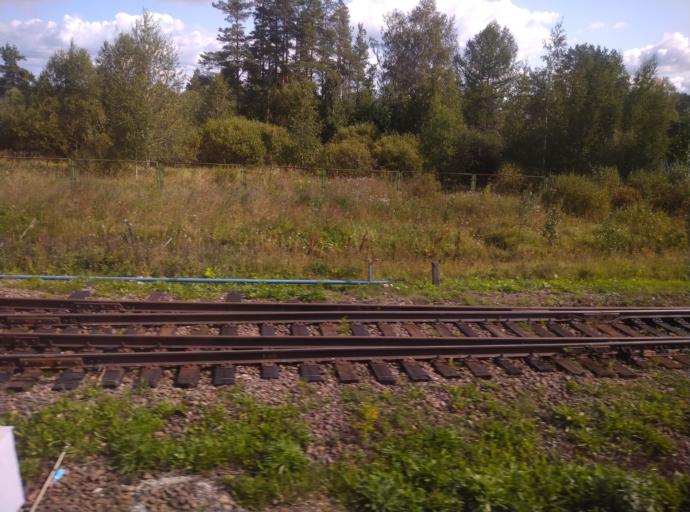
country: RU
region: Leningrad
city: Ul'yanovka
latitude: 59.6249
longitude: 30.7709
